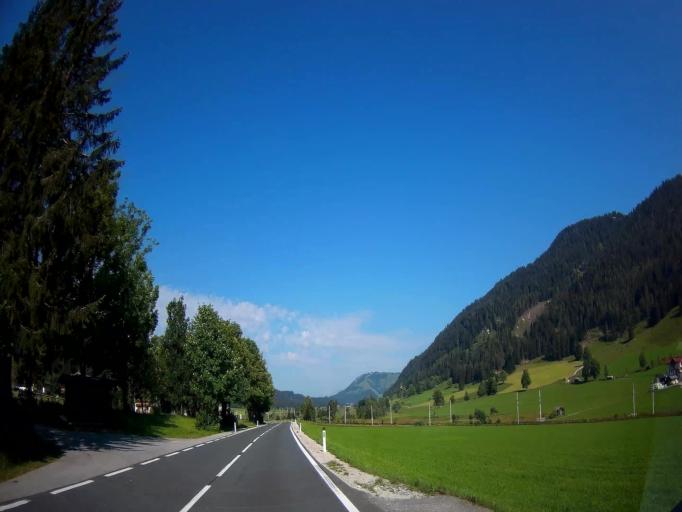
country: AT
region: Tyrol
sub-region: Politischer Bezirk Kitzbuhel
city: Hochfilzen
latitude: 47.4514
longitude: 12.6726
